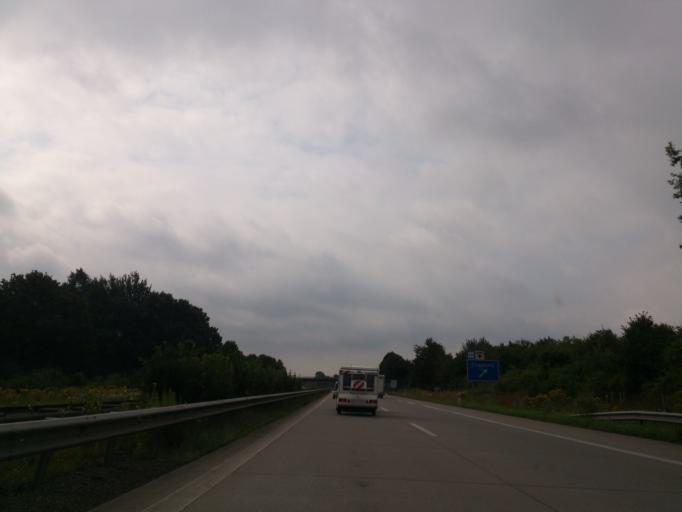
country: DE
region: Schleswig-Holstein
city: Kolln-Reisiek
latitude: 53.7479
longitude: 9.7111
